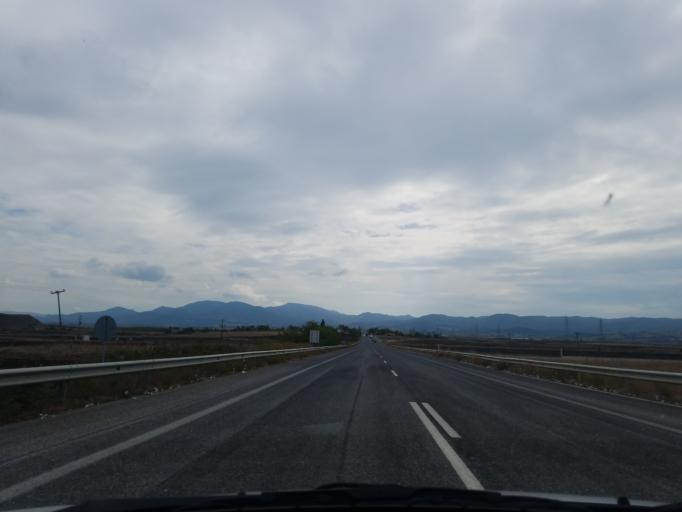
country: GR
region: Central Greece
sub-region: Nomos Fthiotidos
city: Omvriaki
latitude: 39.0822
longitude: 22.3107
